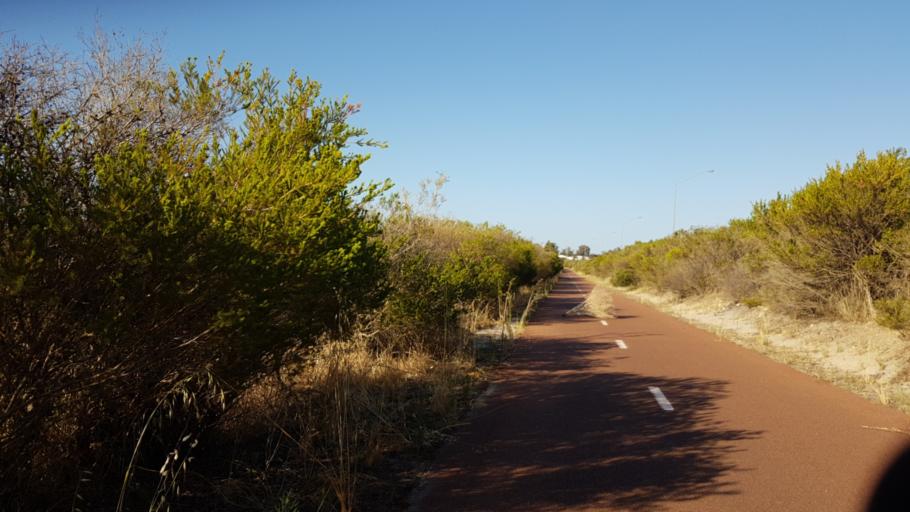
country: AU
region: Western Australia
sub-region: Kwinana
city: Wellard
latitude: -32.2674
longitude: 115.8485
